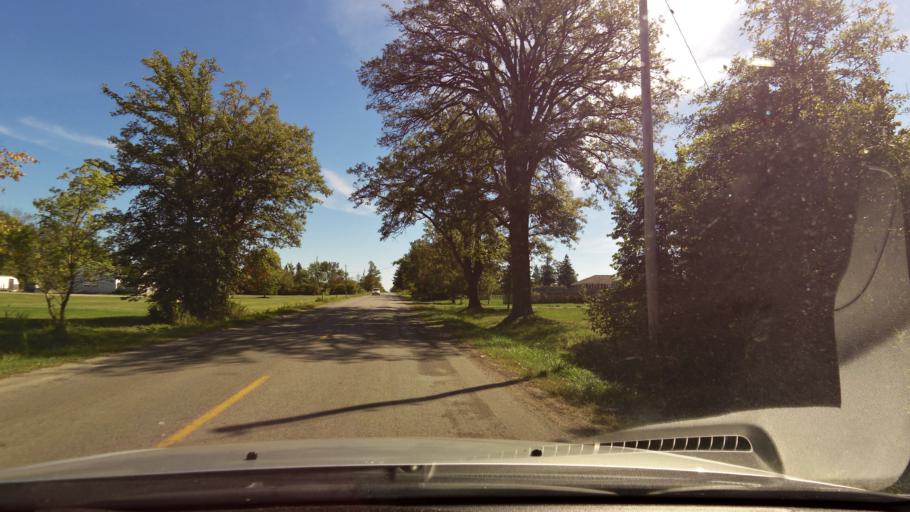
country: CA
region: Ontario
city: Ancaster
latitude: 43.0763
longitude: -80.0823
